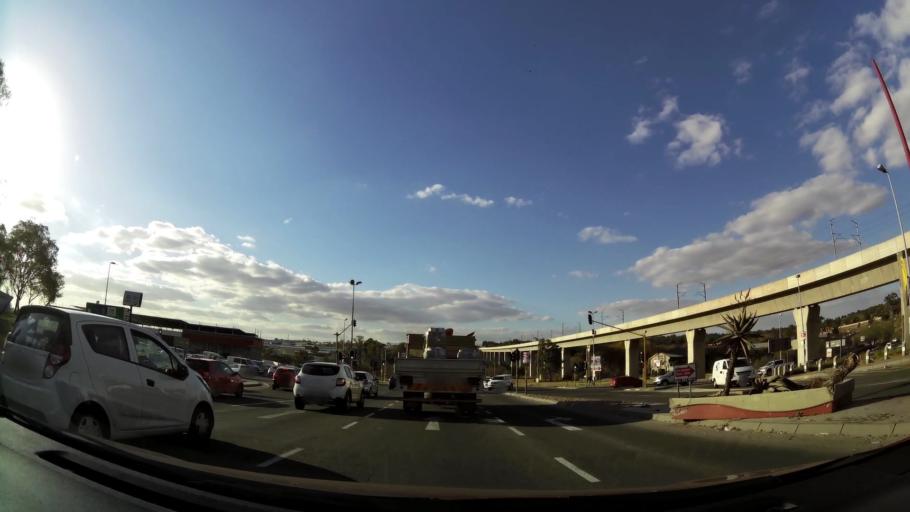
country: ZA
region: Gauteng
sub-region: City of Johannesburg Metropolitan Municipality
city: Midrand
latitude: -25.9566
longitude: 28.1402
